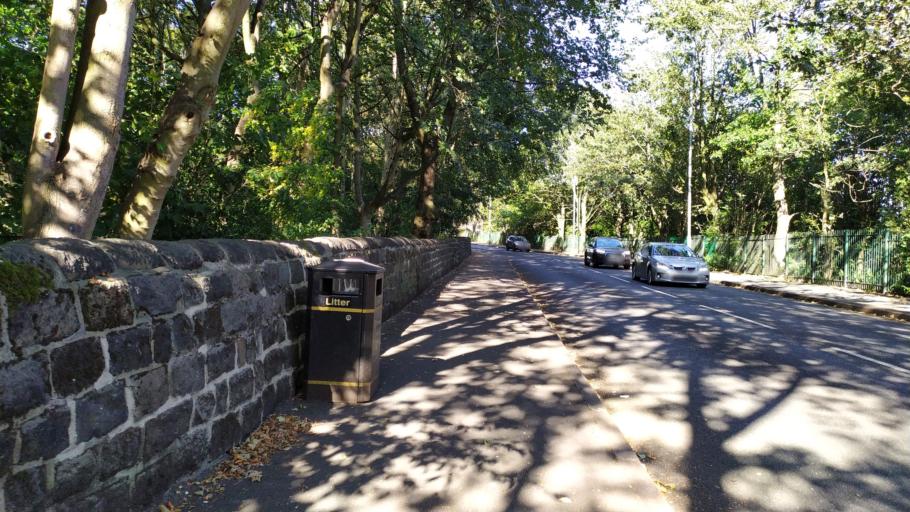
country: GB
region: England
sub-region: City and Borough of Leeds
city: Chapel Allerton
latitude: 53.8362
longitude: -1.5631
